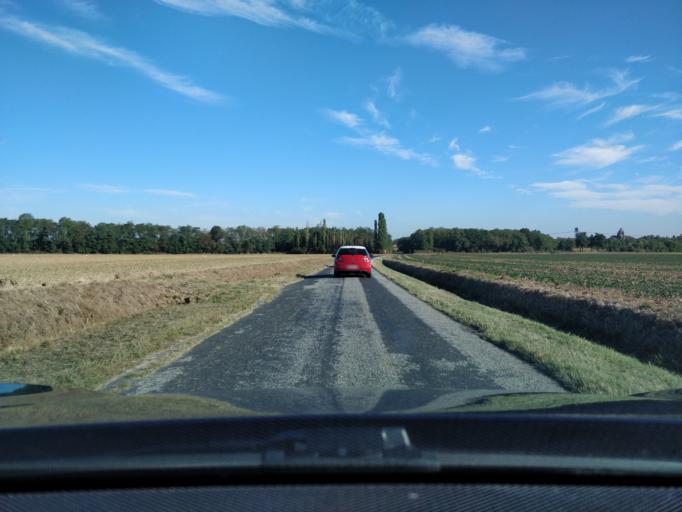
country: FR
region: Ile-de-France
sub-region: Departement de l'Essonne
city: Gometz-la-Ville
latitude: 48.6634
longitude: 2.1161
